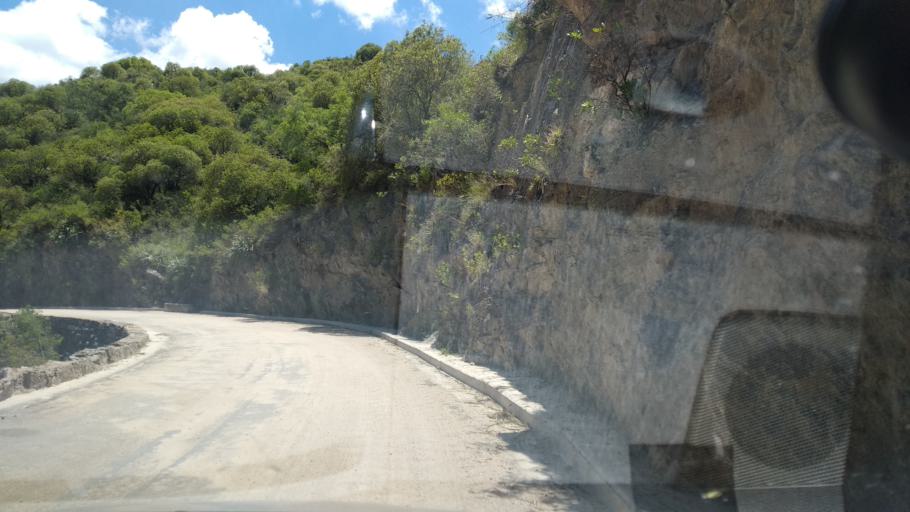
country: AR
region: Cordoba
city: Salsacate
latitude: -31.3757
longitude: -65.3903
